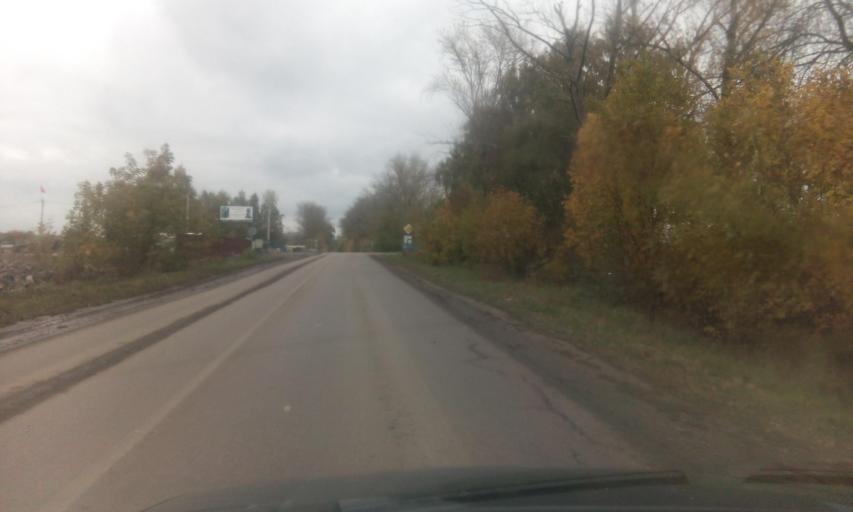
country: RU
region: Tula
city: Uzlovaya
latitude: 53.9745
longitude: 38.1345
